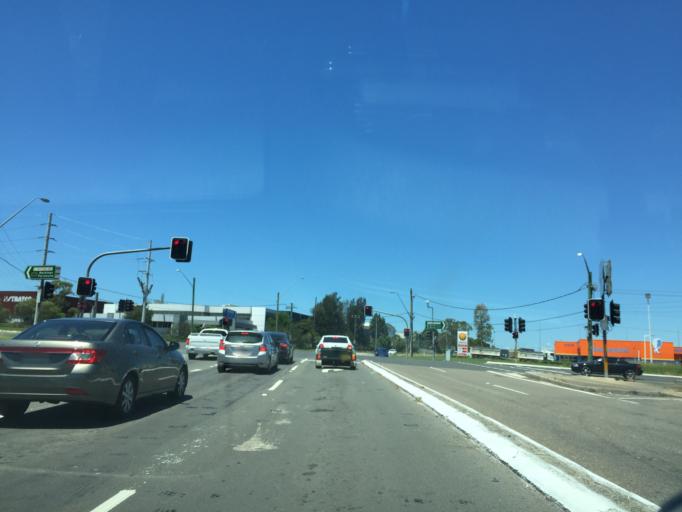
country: AU
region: New South Wales
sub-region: Blacktown
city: Doonside
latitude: -33.7917
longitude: 150.8714
